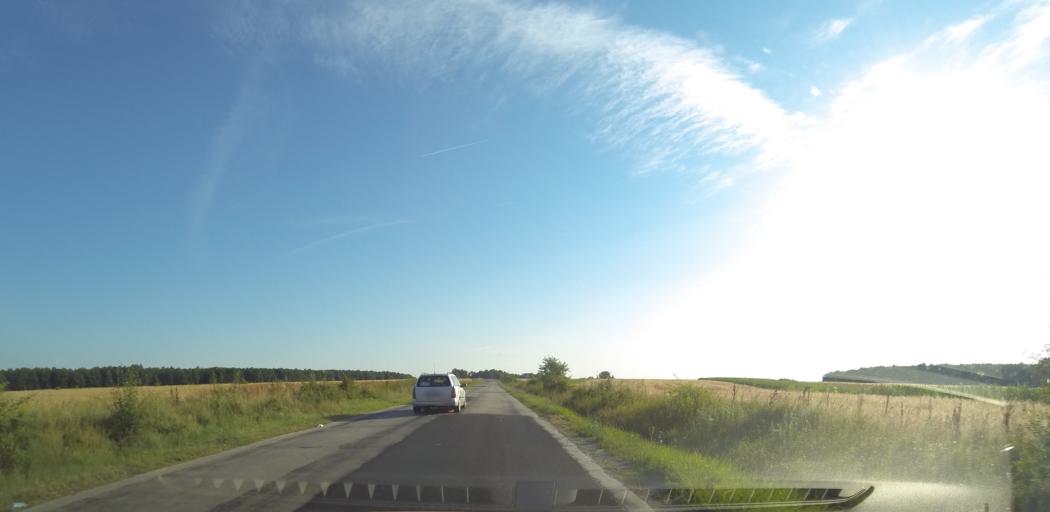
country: RO
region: Valcea
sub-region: Comuna Balcesti
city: Balcesti
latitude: 44.6002
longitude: 23.9282
